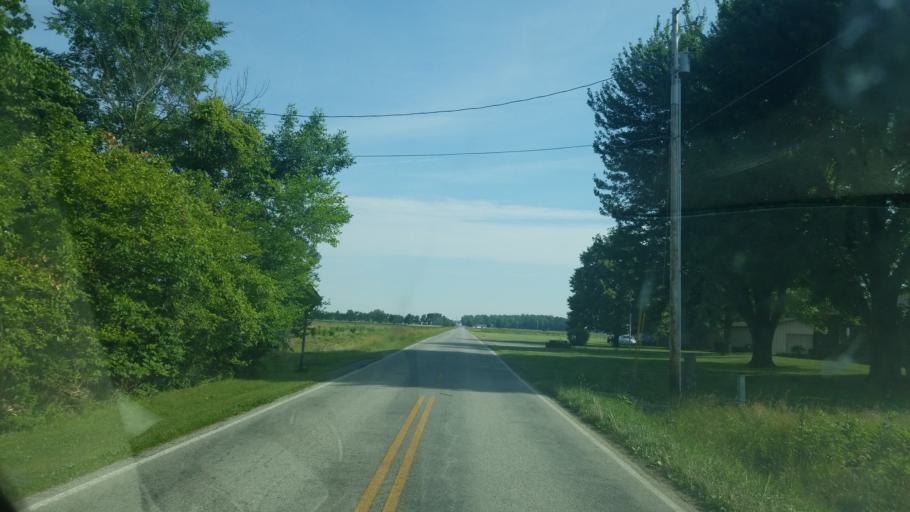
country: US
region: Ohio
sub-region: Hancock County
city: Findlay
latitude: 41.0017
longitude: -83.5882
